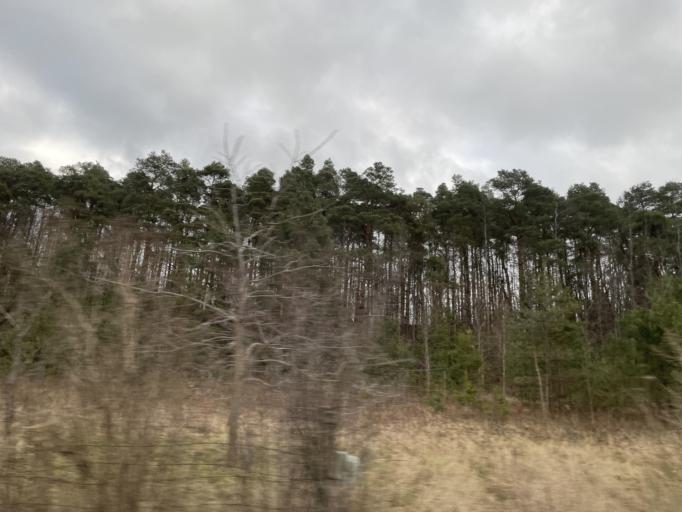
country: CA
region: Ontario
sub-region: Wellington County
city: Guelph
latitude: 43.4968
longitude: -80.3445
